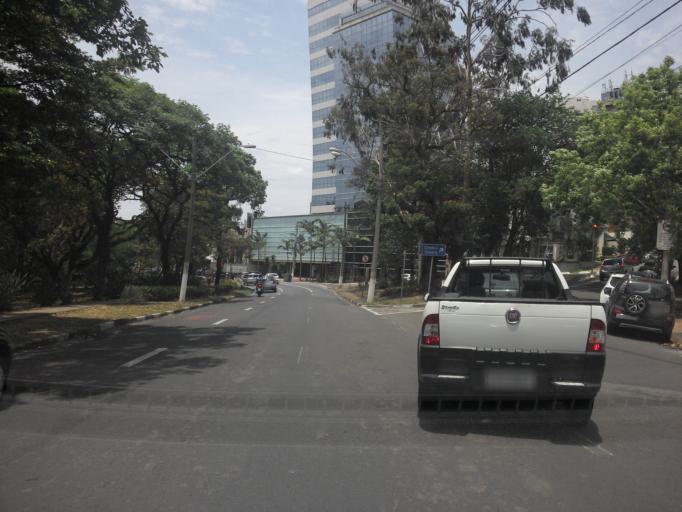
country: BR
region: Sao Paulo
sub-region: Campinas
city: Campinas
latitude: -22.9036
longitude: -47.0478
